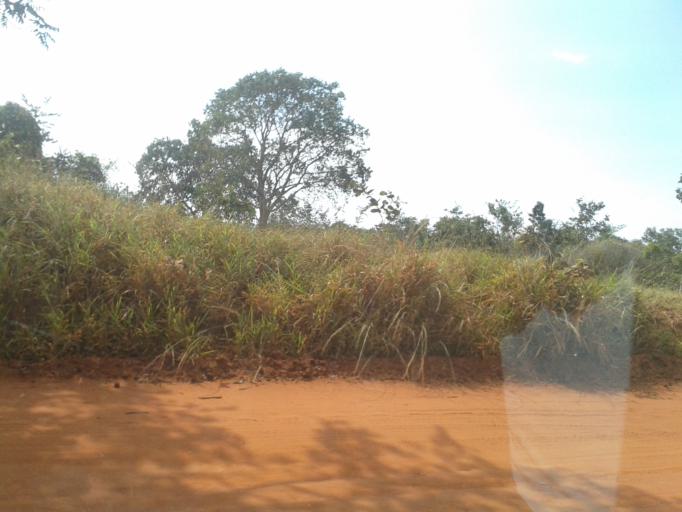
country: BR
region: Minas Gerais
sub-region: Ituiutaba
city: Ituiutaba
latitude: -19.0567
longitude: -49.3626
